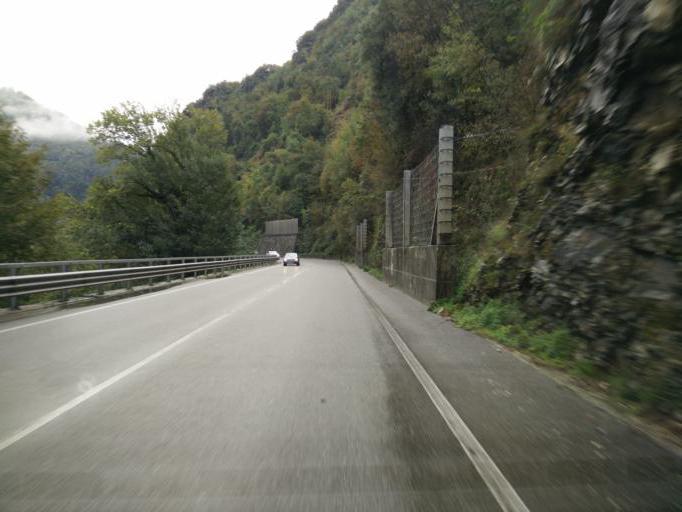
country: IT
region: Tuscany
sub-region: Provincia di Lucca
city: Valdottavo
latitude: 43.9353
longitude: 10.4997
